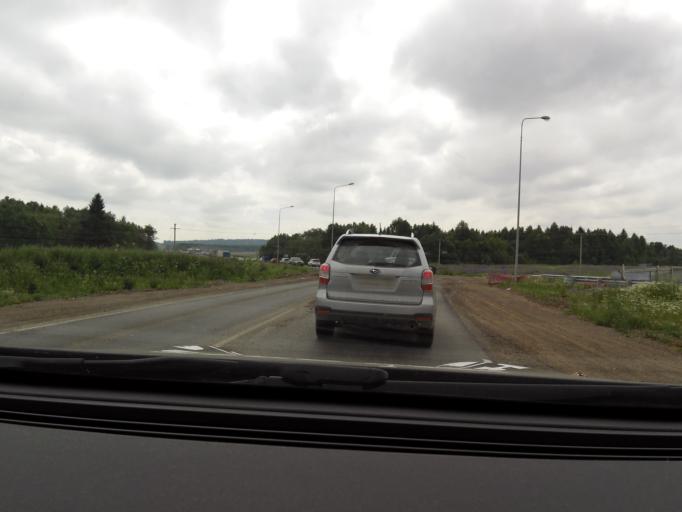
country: RU
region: Perm
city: Zvezdnyy
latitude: 57.7805
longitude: 56.3452
